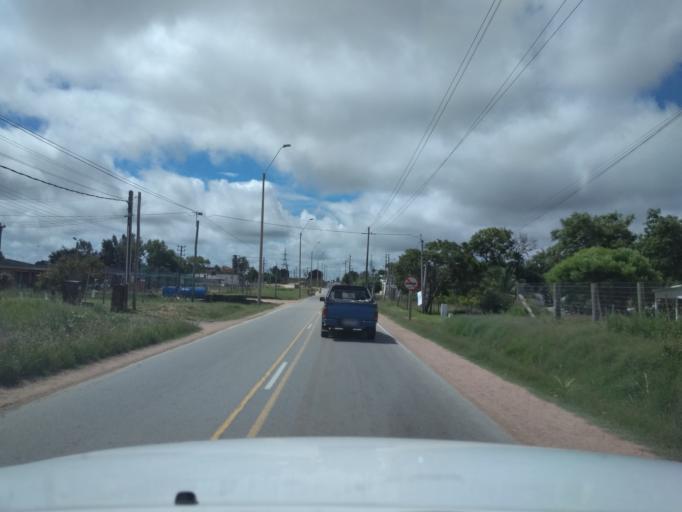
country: UY
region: Canelones
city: Pando
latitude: -34.7030
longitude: -55.9659
